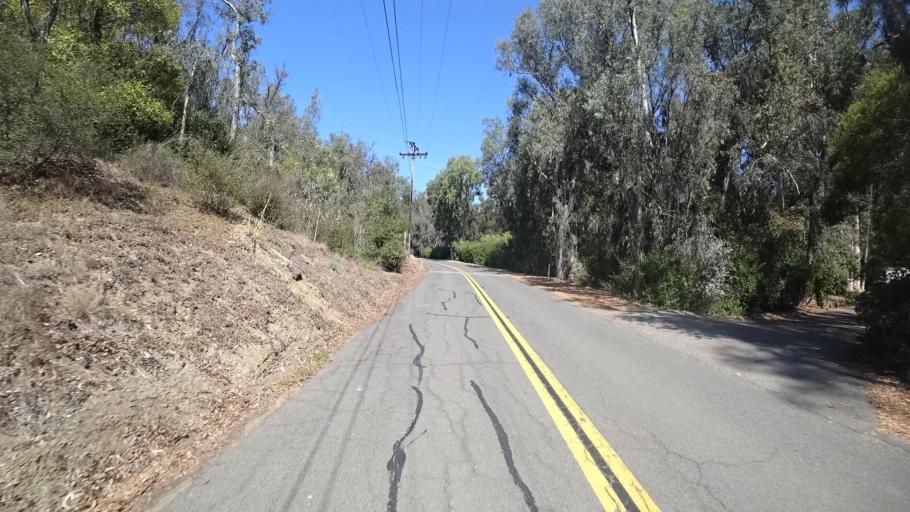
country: US
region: California
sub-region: San Diego County
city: Rancho Santa Fe
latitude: 33.0000
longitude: -117.2155
